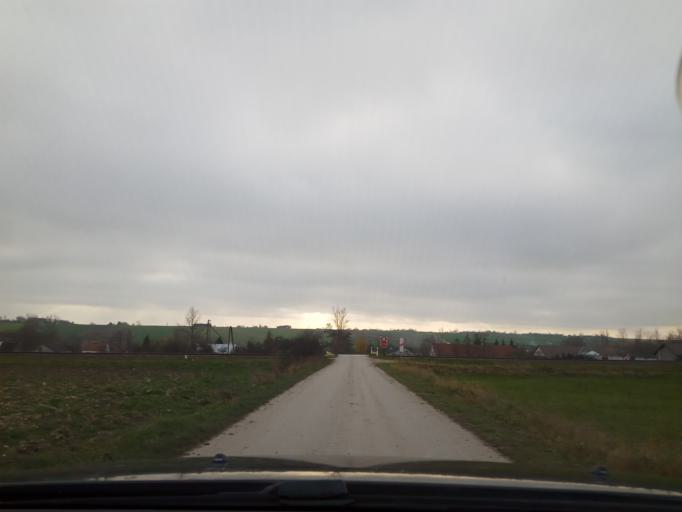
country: PL
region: Swietokrzyskie
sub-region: Powiat jedrzejowski
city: Imielno
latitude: 50.6125
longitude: 20.3916
